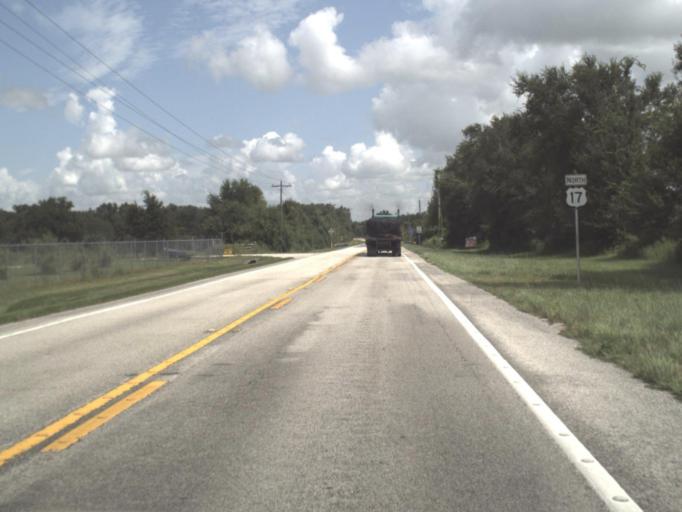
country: US
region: Florida
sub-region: DeSoto County
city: Arcadia
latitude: 27.3407
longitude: -81.8056
